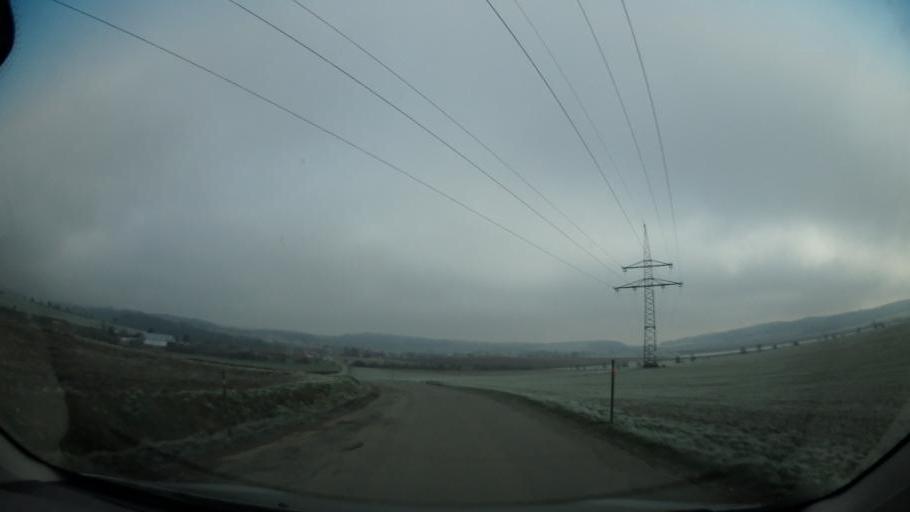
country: CZ
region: Vysocina
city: Mohelno
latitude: 49.1210
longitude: 16.2312
